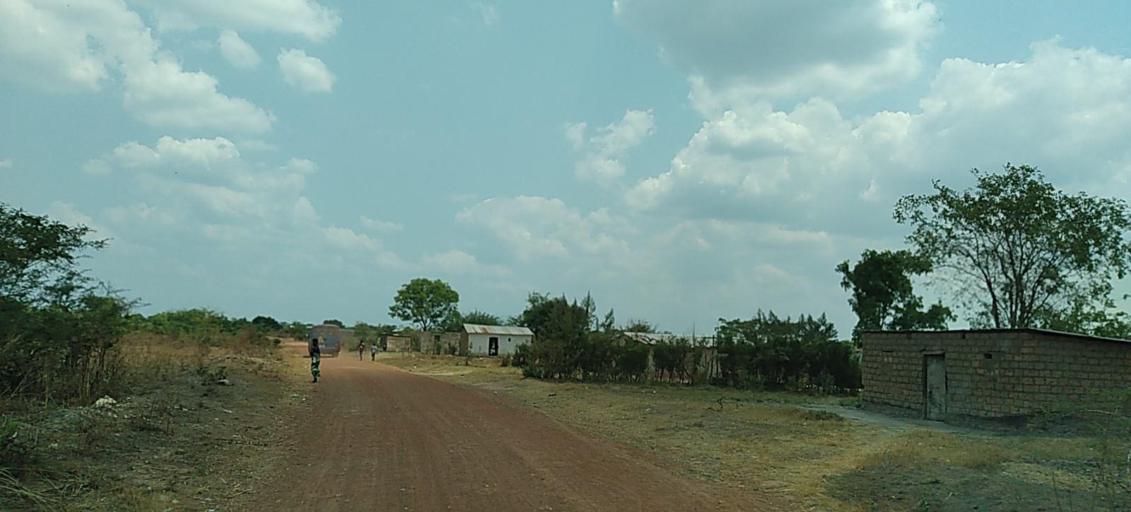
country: ZM
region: Copperbelt
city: Luanshya
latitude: -13.1265
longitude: 28.3105
